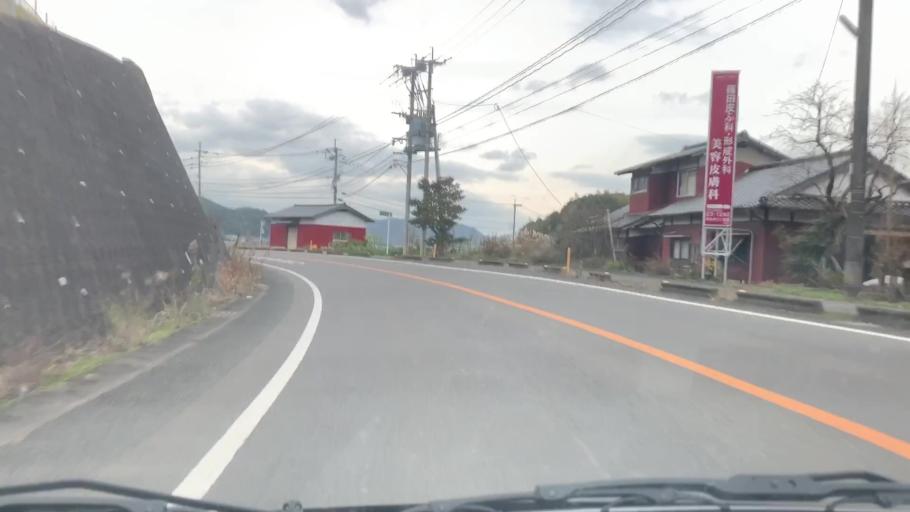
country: JP
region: Saga Prefecture
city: Takeocho-takeo
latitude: 33.1658
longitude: 130.0588
